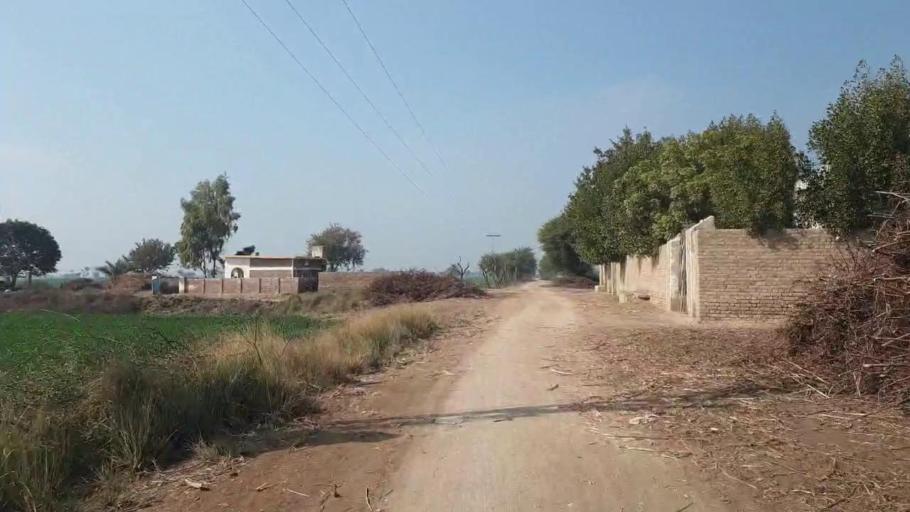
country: PK
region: Sindh
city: Shahdadpur
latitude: 26.0267
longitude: 68.5699
